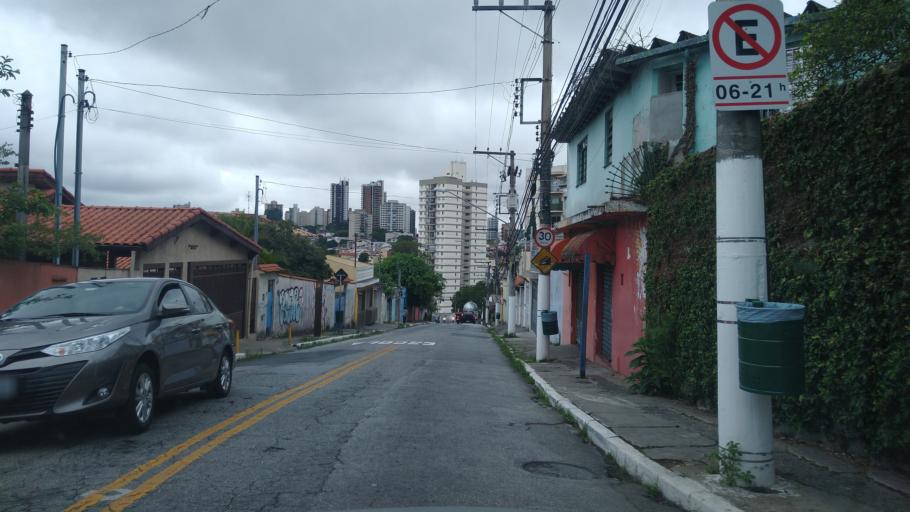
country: BR
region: Sao Paulo
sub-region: Sao Paulo
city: Sao Paulo
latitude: -23.4755
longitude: -46.6234
